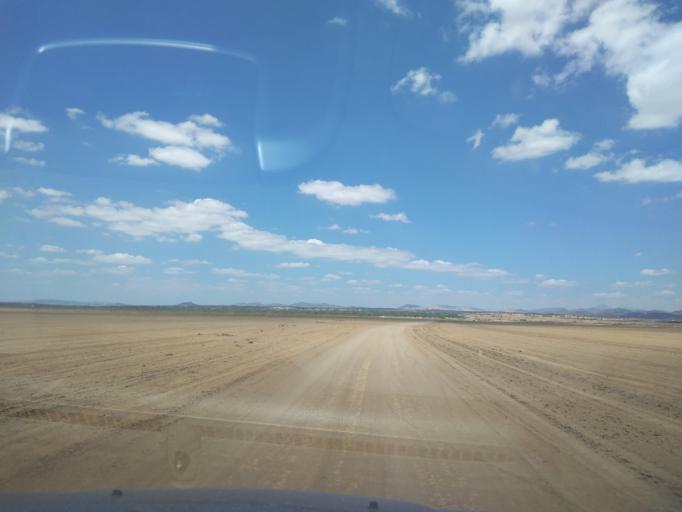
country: TN
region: Susah
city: Harqalah
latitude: 36.1626
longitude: 10.4553
